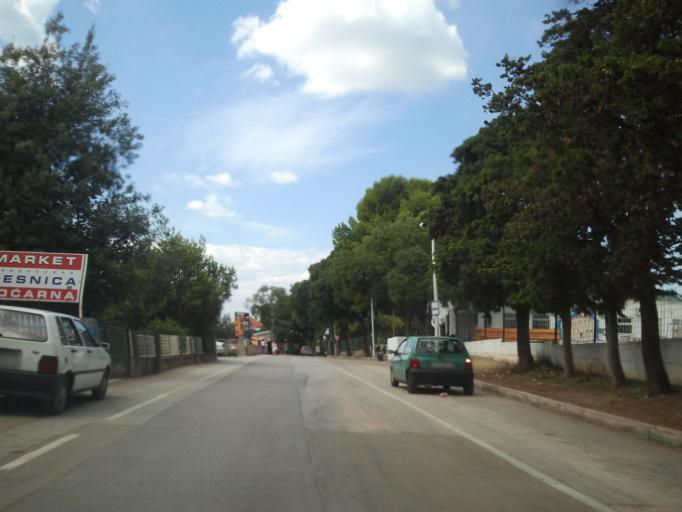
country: HR
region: Zadarska
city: Zadar
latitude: 44.1268
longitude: 15.2254
